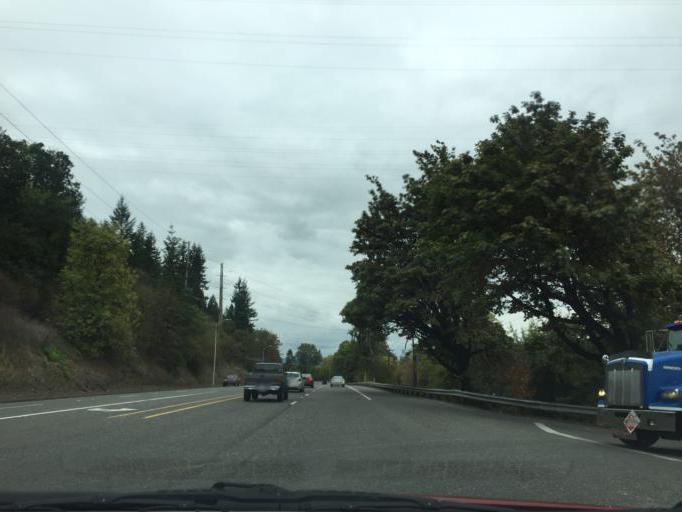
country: US
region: Oregon
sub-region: Washington County
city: Oak Hills
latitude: 45.6103
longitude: -122.7957
